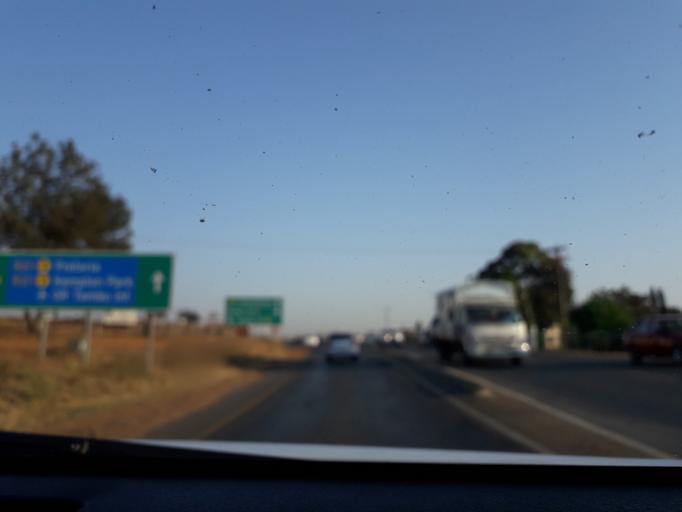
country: ZA
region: Gauteng
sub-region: Ekurhuleni Metropolitan Municipality
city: Tembisa
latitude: -26.0758
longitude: 28.2848
